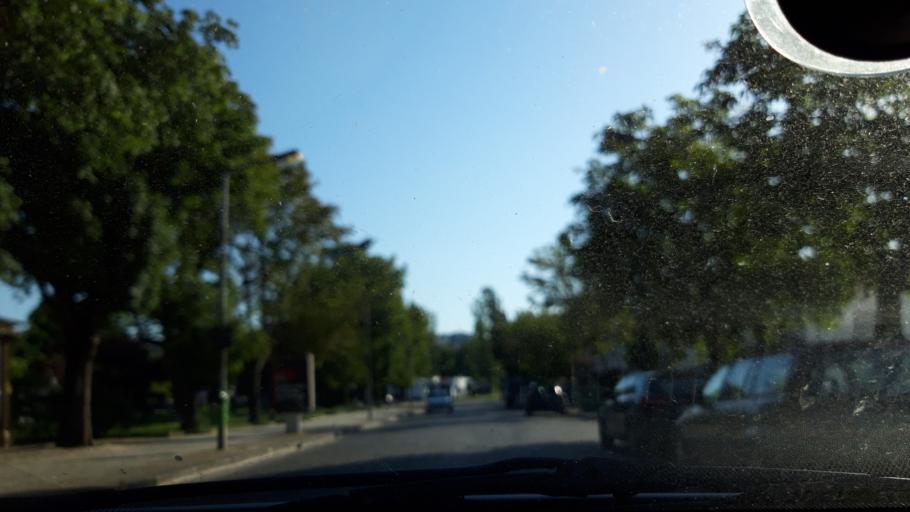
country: PT
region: Santarem
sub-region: Torres Novas
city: Torres Novas
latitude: 39.4813
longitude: -8.5408
